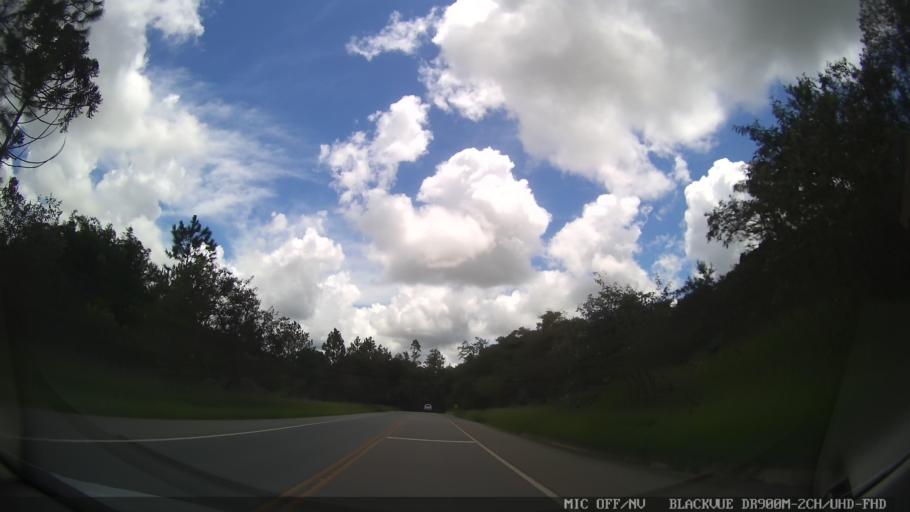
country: BR
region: Sao Paulo
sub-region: Amparo
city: Amparo
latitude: -22.7784
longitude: -46.7341
